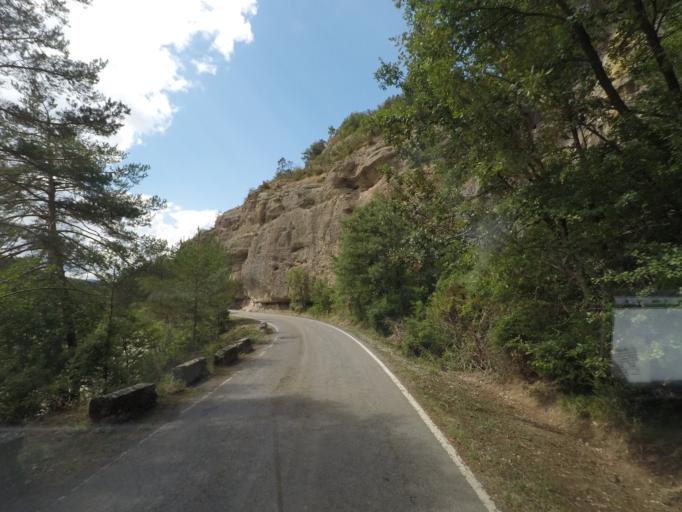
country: ES
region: Aragon
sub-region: Provincia de Huesca
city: Yebra de Basa
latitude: 42.4044
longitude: -0.2406
